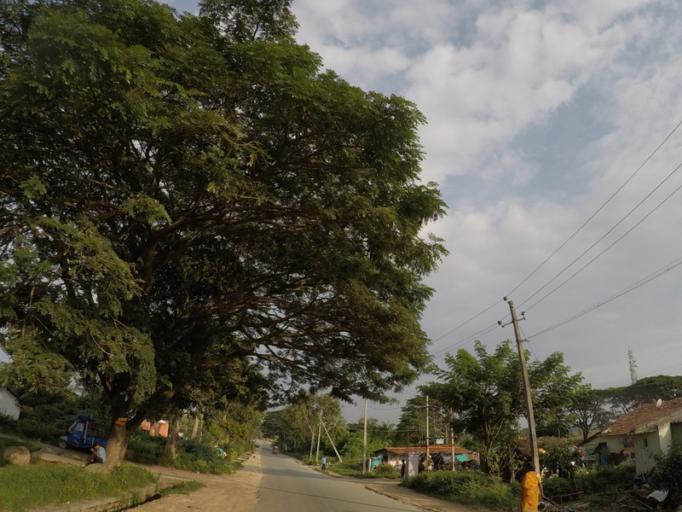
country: IN
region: Karnataka
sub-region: Chikmagalur
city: Chikmagalur
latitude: 13.2664
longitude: 75.8371
